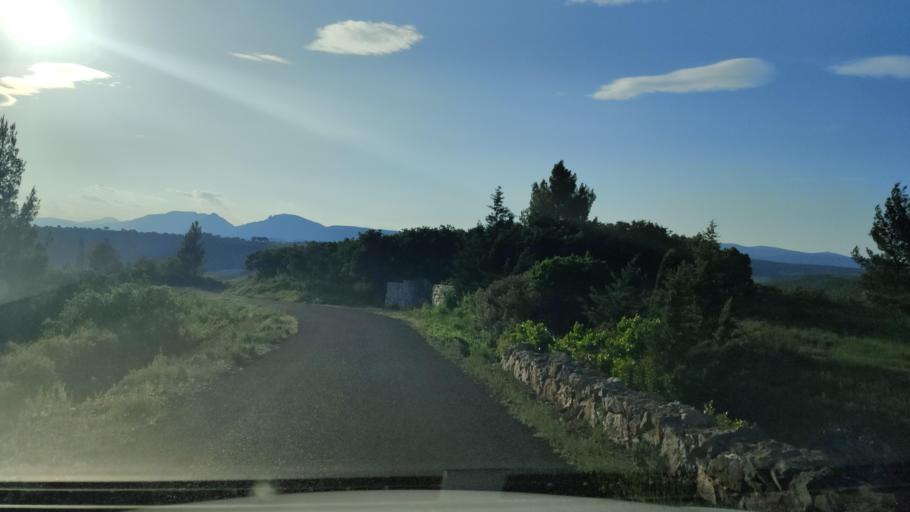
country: FR
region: Languedoc-Roussillon
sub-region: Departement des Pyrenees-Orientales
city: Estagel
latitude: 42.7985
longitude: 2.7246
